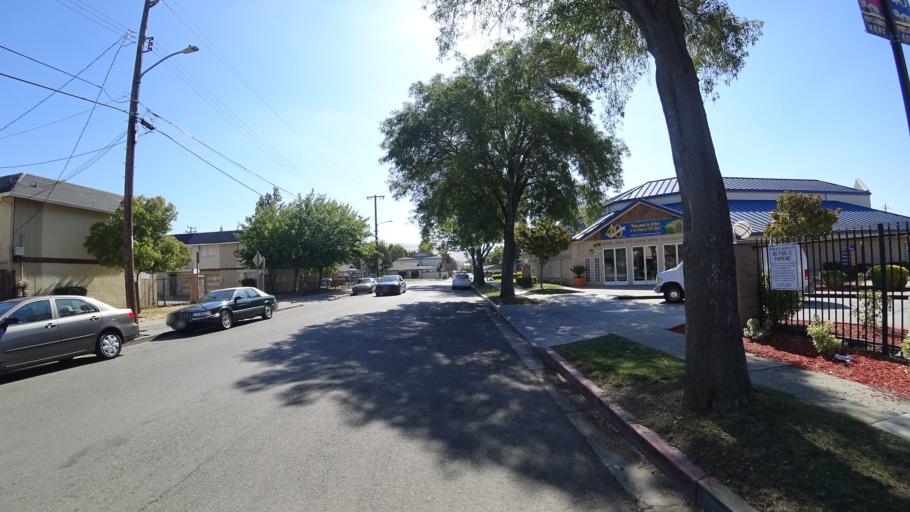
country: US
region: California
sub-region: Alameda County
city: Hayward
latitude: 37.6333
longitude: -122.0728
